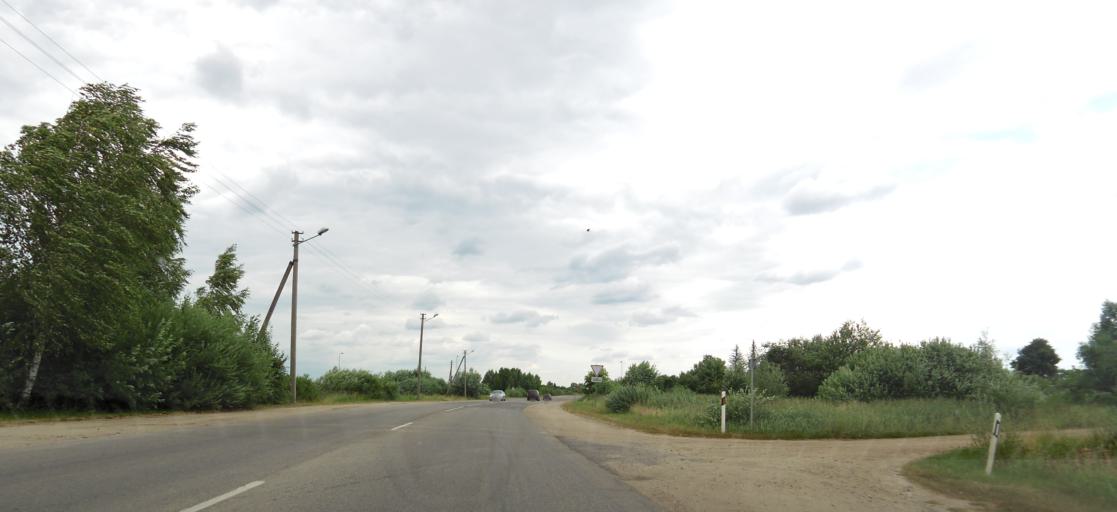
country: LT
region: Vilnius County
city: Ukmerge
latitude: 55.2549
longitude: 24.7438
